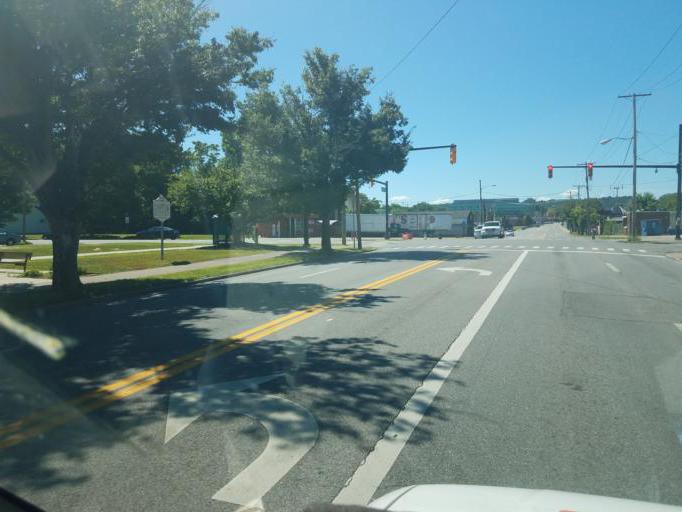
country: US
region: West Virginia
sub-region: Cabell County
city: Huntington
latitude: 38.4163
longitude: -82.4301
